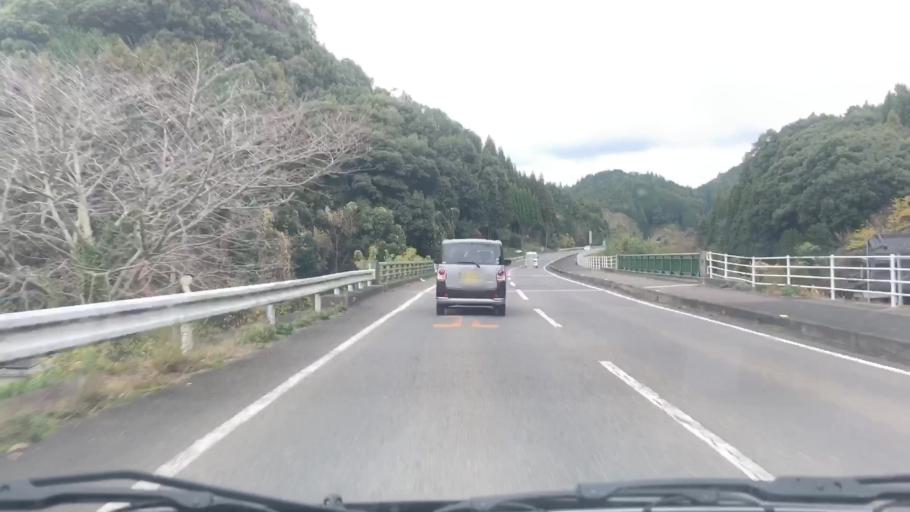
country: JP
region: Saga Prefecture
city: Ureshinomachi-shimojuku
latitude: 33.0935
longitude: 130.0286
